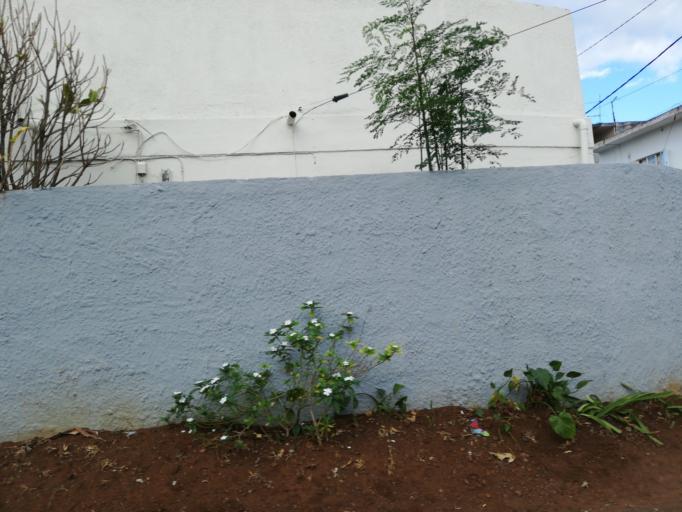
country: MU
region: Black River
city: Petite Riviere
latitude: -20.2227
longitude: 57.4622
